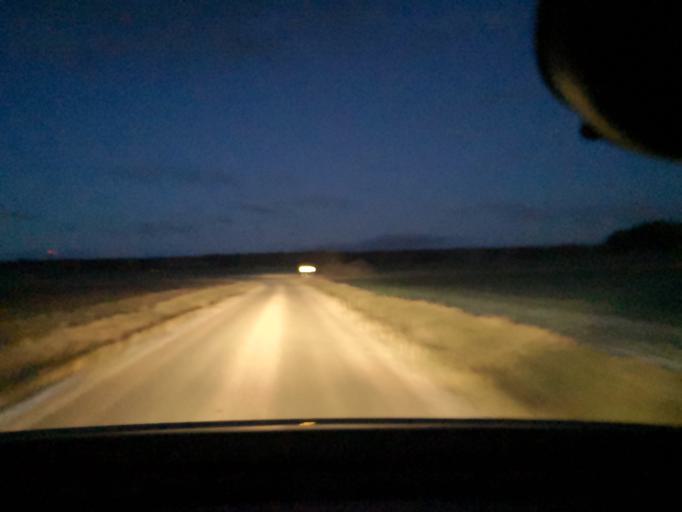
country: SE
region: Uppsala
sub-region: Heby Kommun
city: Heby
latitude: 59.9229
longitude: 16.7530
